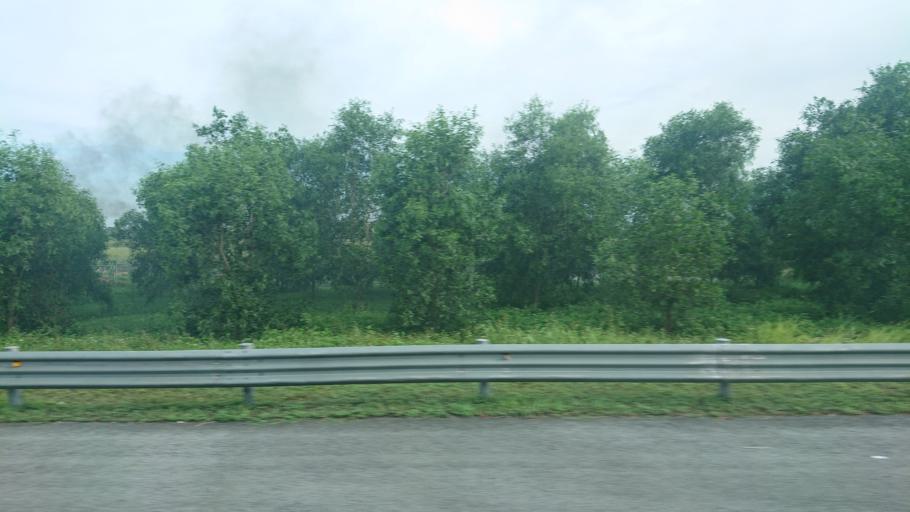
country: VN
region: Hai Phong
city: Nui Doi
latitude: 20.7656
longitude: 106.6550
